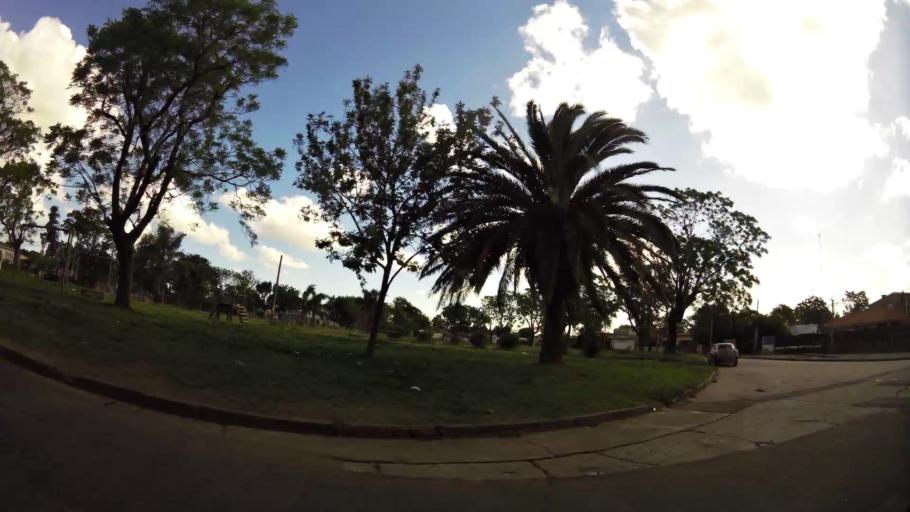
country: UY
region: Canelones
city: La Paz
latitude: -34.8099
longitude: -56.2249
